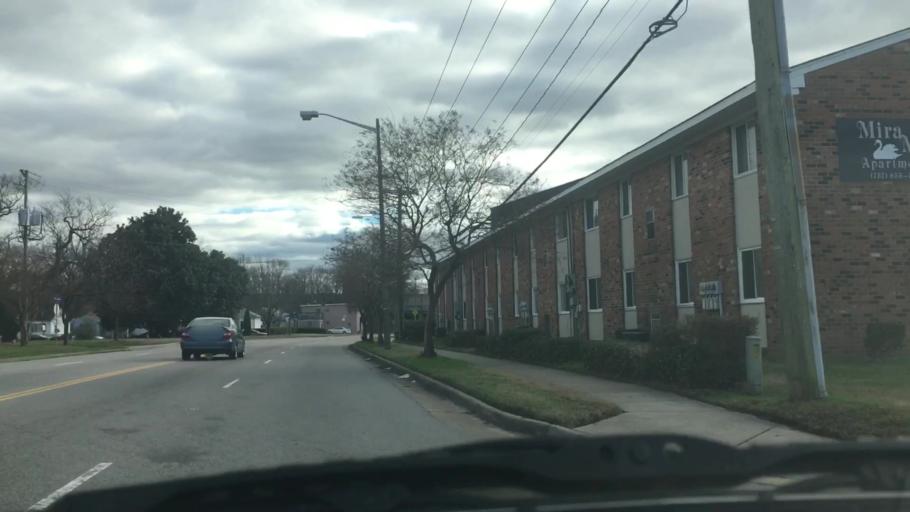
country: US
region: Virginia
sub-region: City of Norfolk
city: Norfolk
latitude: 36.9055
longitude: -76.2435
